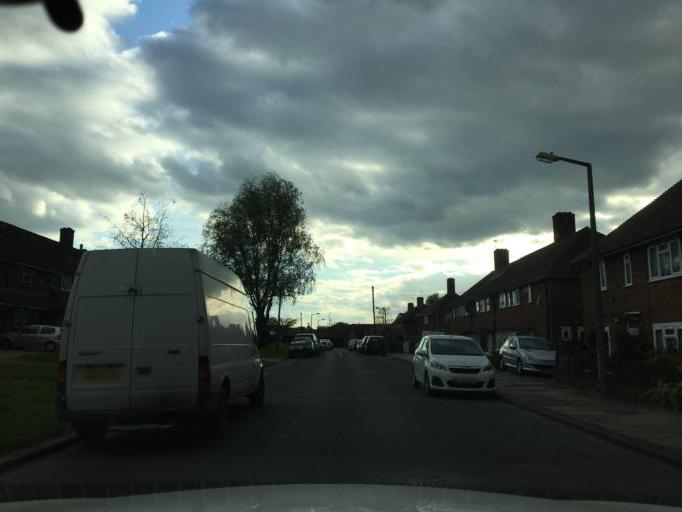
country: GB
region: England
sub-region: Greater London
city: Chislehurst
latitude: 51.4311
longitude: 0.0544
